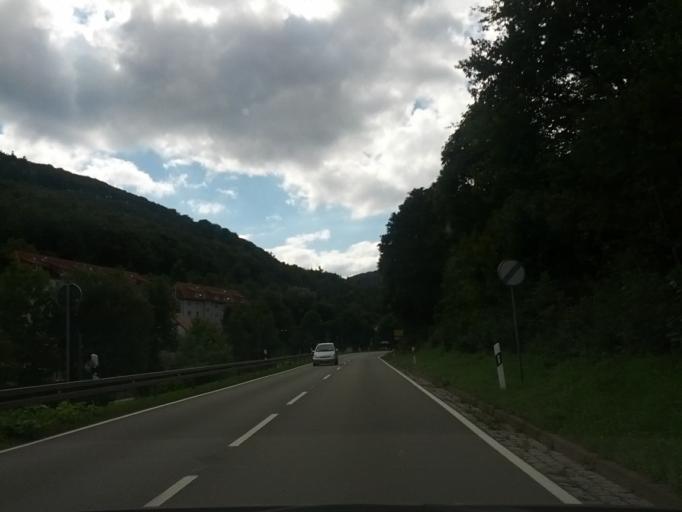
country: DE
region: Thuringia
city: Ruhla
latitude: 50.9062
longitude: 10.3747
